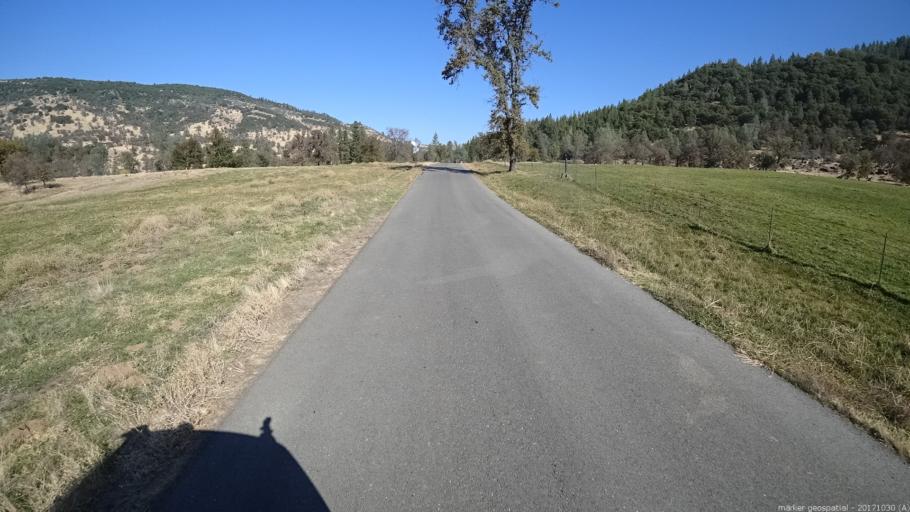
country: US
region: California
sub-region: Shasta County
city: Shingletown
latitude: 40.5517
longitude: -121.9111
